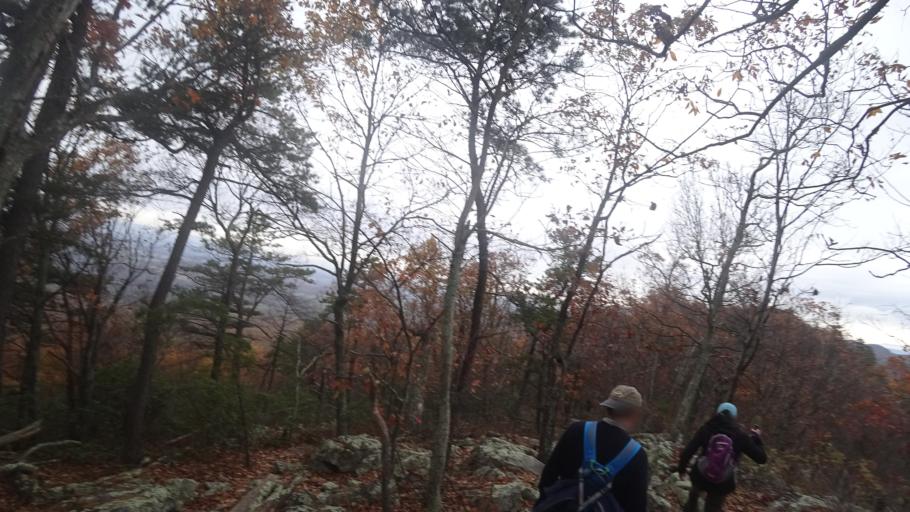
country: US
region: Virginia
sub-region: Rockingham County
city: Massanutten
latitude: 38.4118
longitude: -78.7613
